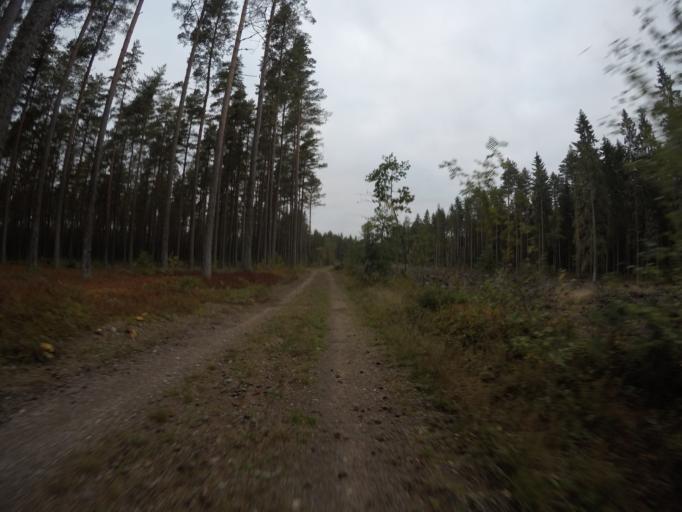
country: SE
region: Vaestmanland
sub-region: Kungsors Kommun
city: Kungsoer
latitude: 59.3435
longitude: 16.1191
